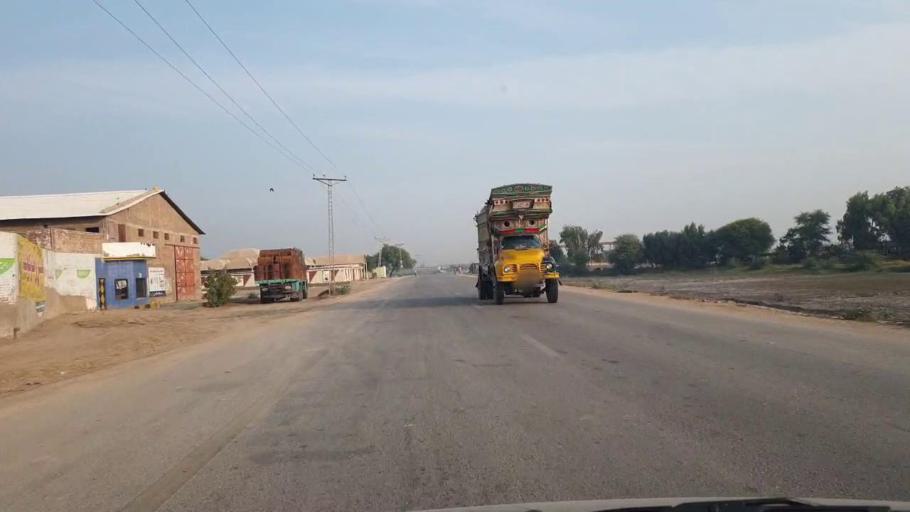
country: PK
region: Sindh
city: Badin
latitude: 24.6871
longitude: 68.8238
